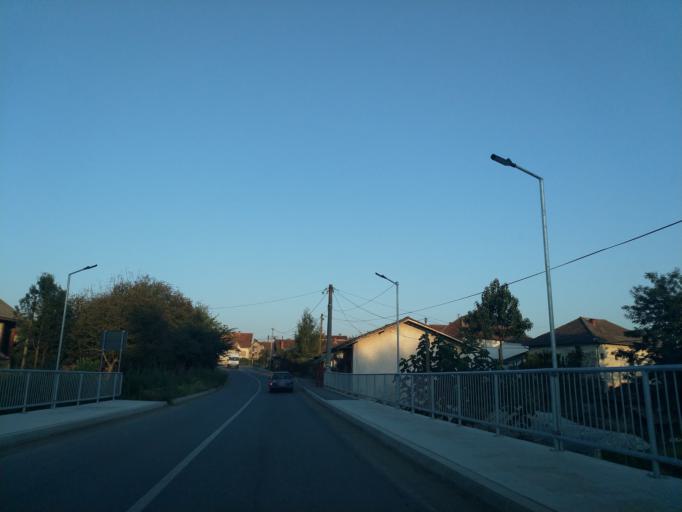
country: RS
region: Central Serbia
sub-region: Rasinski Okrug
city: Trstenik
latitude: 43.6311
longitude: 21.0762
